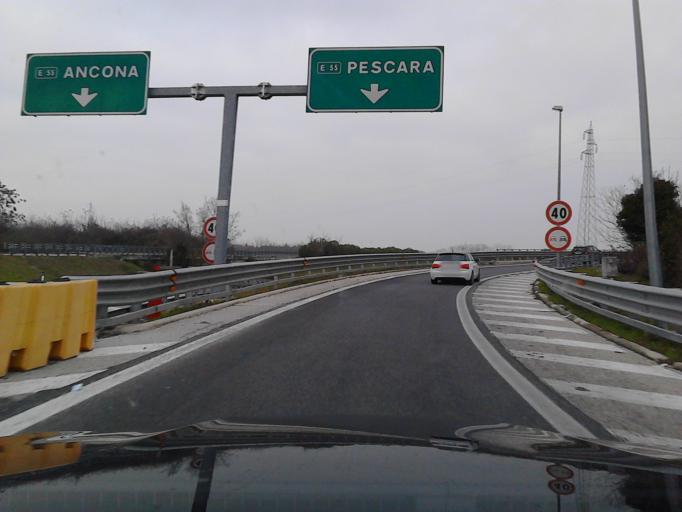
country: IT
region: Abruzzo
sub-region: Provincia di Teramo
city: Villa Rosa
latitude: 42.8378
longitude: 13.9011
